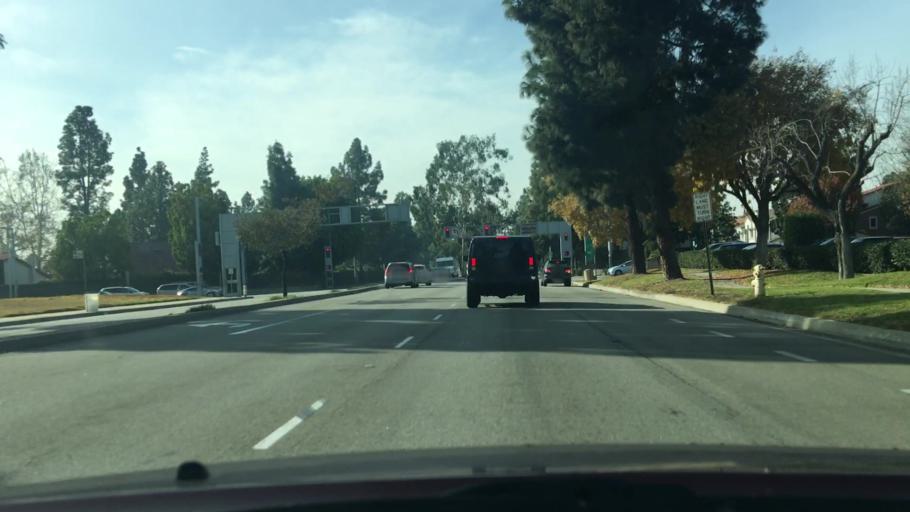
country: US
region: California
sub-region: Los Angeles County
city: Cerritos
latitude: 33.8733
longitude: -118.0542
